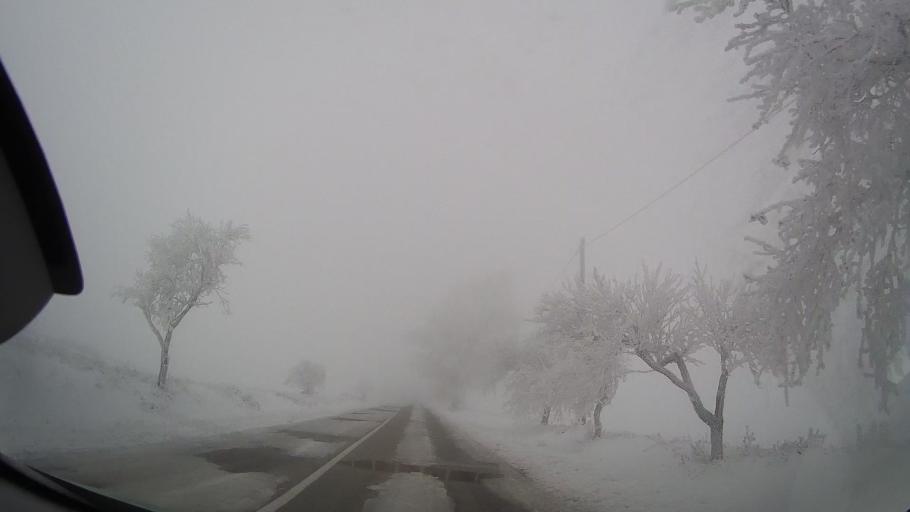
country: RO
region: Neamt
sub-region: Comuna Valea Ursului
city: Valea Ursului
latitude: 46.8044
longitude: 27.0719
